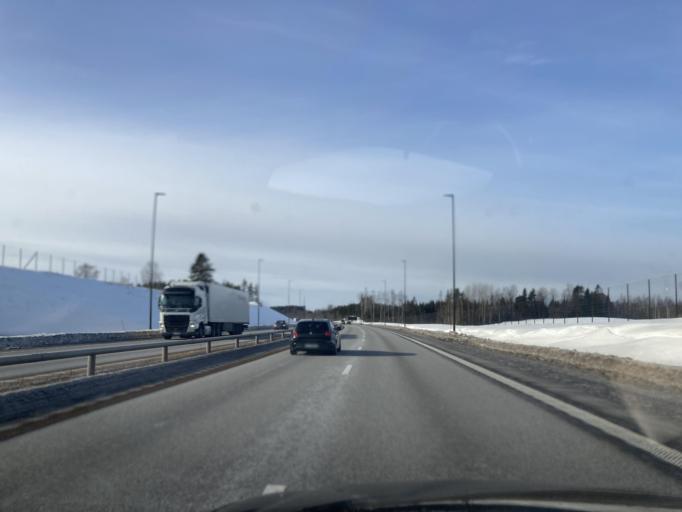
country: NO
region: Hedmark
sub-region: Loten
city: Loten
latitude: 60.8384
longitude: 11.3134
